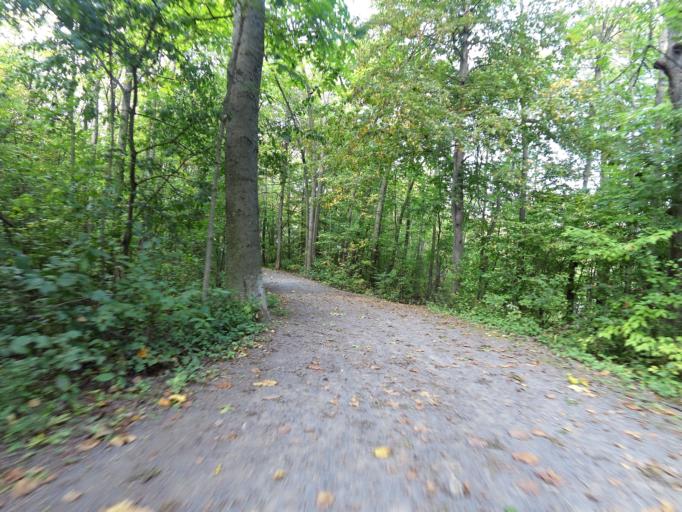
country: CA
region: Ontario
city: Bells Corners
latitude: 45.2645
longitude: -75.7211
